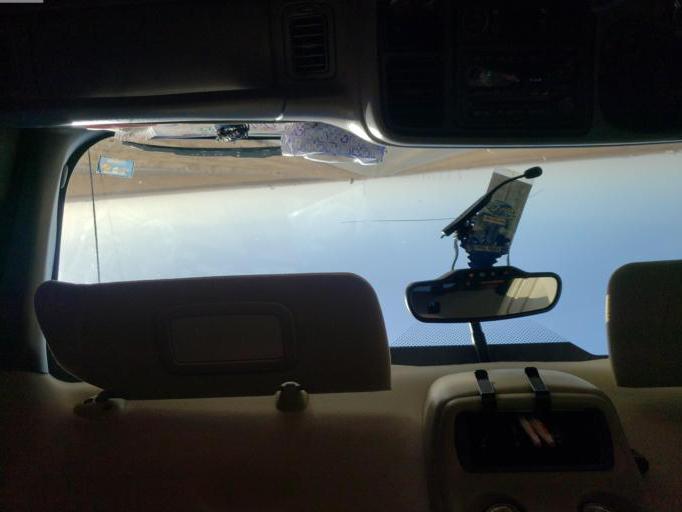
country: US
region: Kansas
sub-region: Finney County
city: Garden City
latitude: 37.7630
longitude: -100.8712
